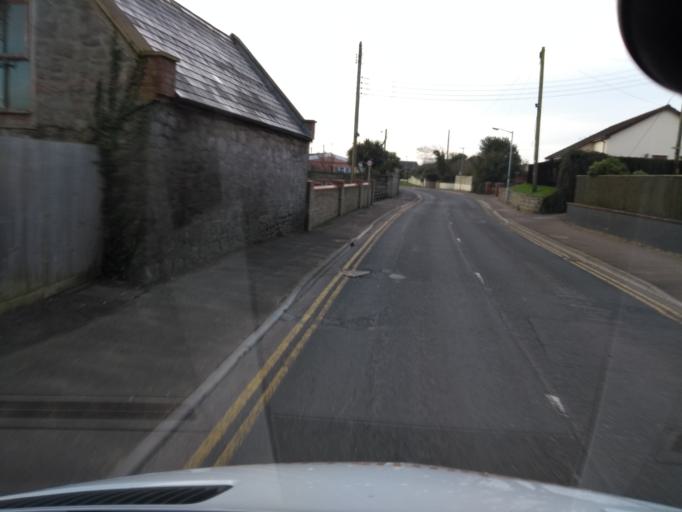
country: GB
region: England
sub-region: Somerset
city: Burnham-on-Sea
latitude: 51.2944
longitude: -3.0104
